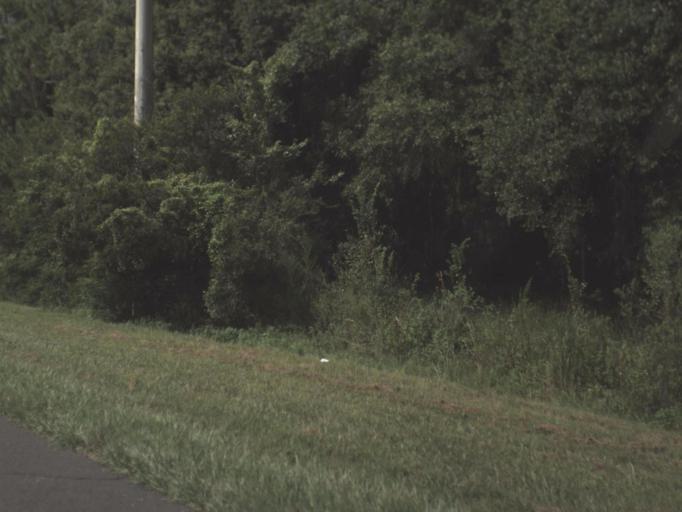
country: US
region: Florida
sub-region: Pasco County
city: Crystal Springs
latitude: 28.1430
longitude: -82.1506
